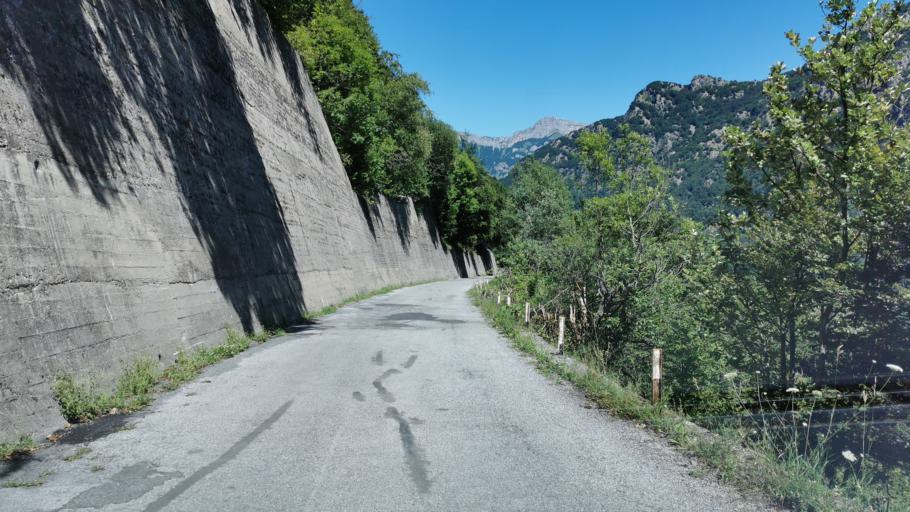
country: IT
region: Piedmont
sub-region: Provincia di Cuneo
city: Entracque
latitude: 44.2047
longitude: 7.3703
